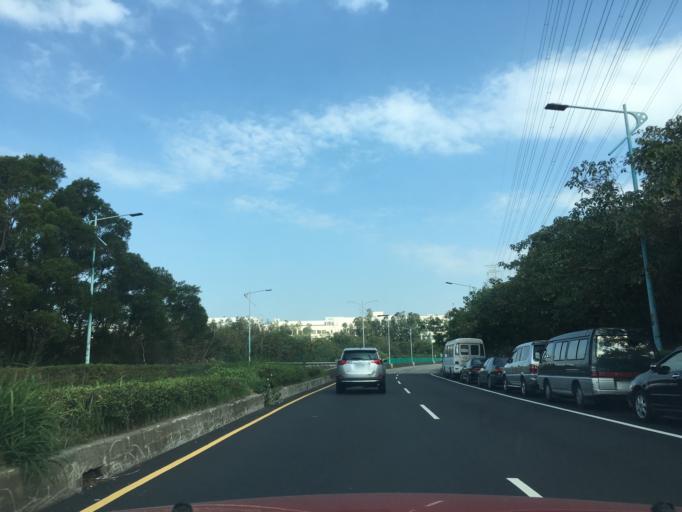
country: TW
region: Taiwan
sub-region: Hsinchu
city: Hsinchu
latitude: 24.7685
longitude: 121.0081
